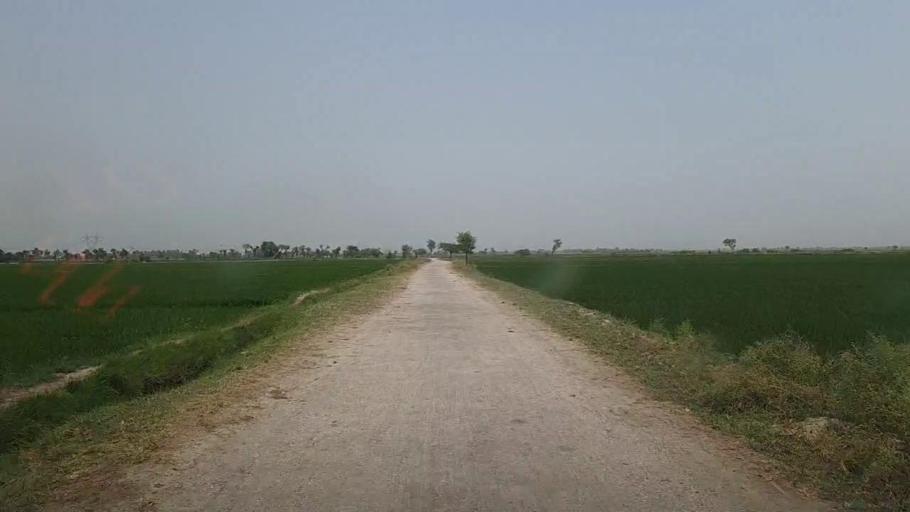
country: PK
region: Sindh
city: Sita Road
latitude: 27.0594
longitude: 67.8489
